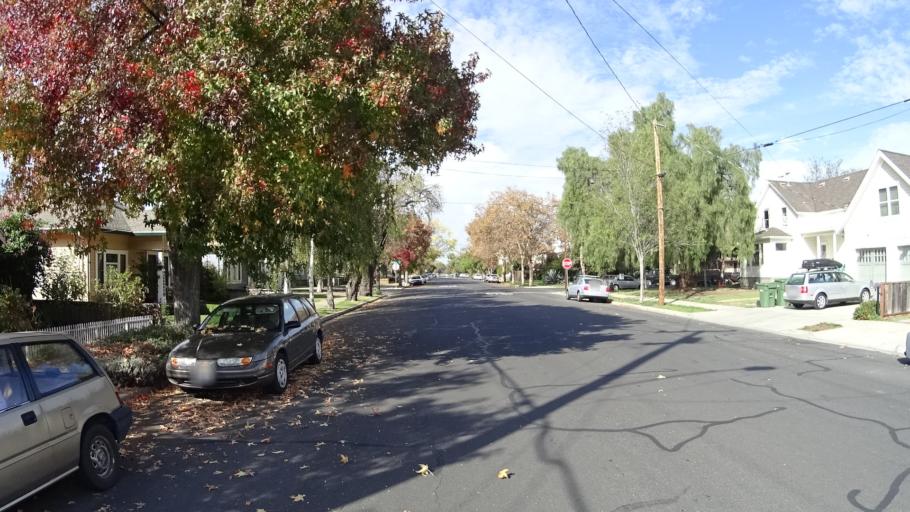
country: US
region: California
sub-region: Santa Clara County
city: Santa Clara
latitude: 37.3444
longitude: -121.9487
